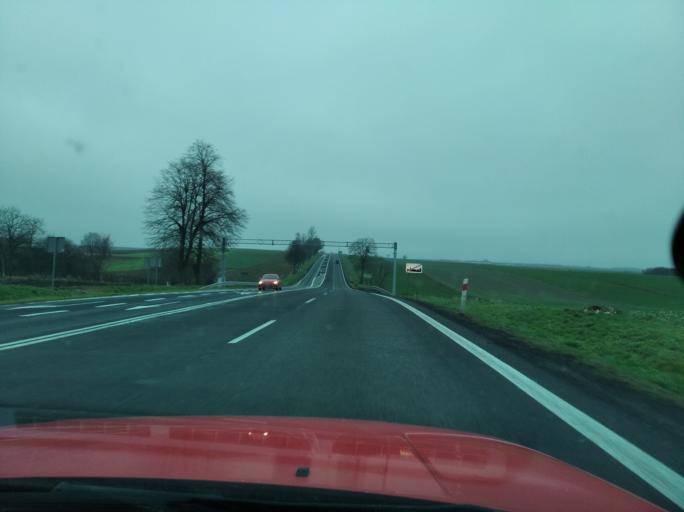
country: PL
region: Subcarpathian Voivodeship
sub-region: Powiat jaroslawski
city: Wierzbna
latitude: 50.0337
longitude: 22.5974
